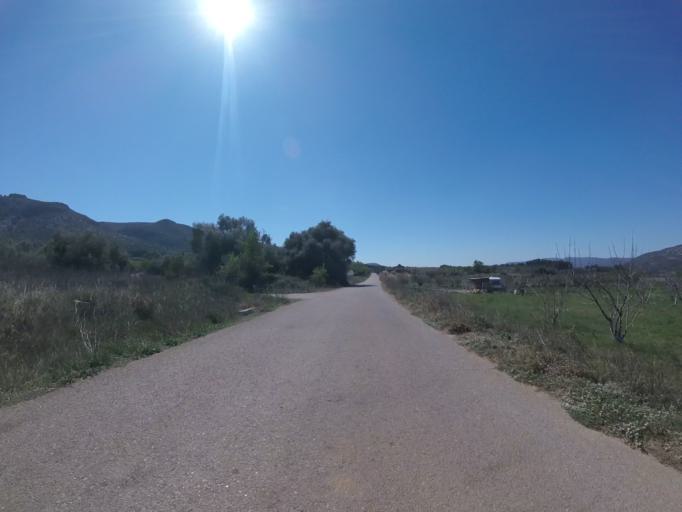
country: ES
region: Valencia
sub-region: Provincia de Castello
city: Cervera del Maestre
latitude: 40.4096
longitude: 0.1753
